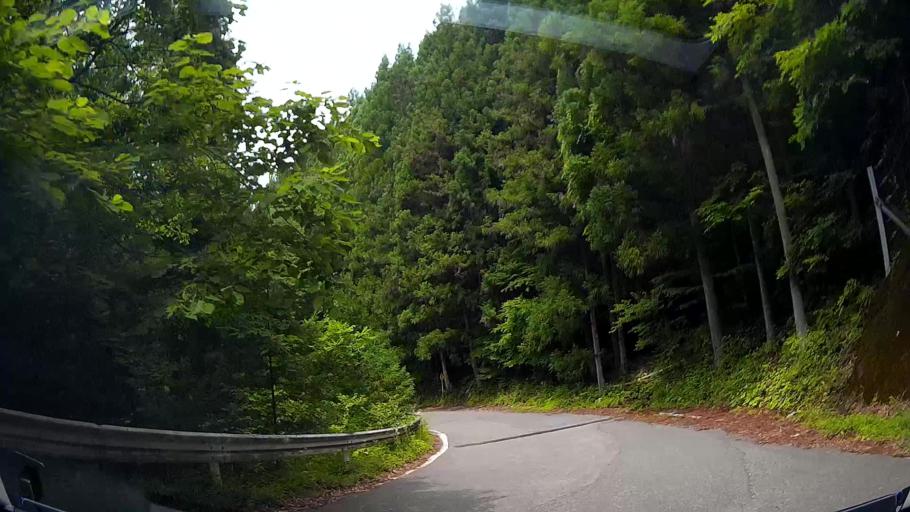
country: JP
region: Nagano
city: Iida
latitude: 35.2849
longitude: 137.9178
